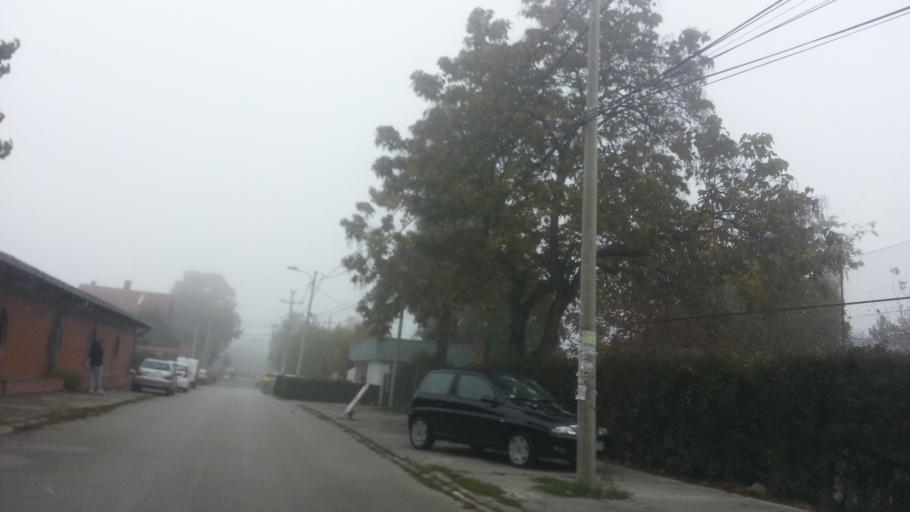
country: RS
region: Central Serbia
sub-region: Belgrade
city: Zemun
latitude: 44.8564
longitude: 20.3876
